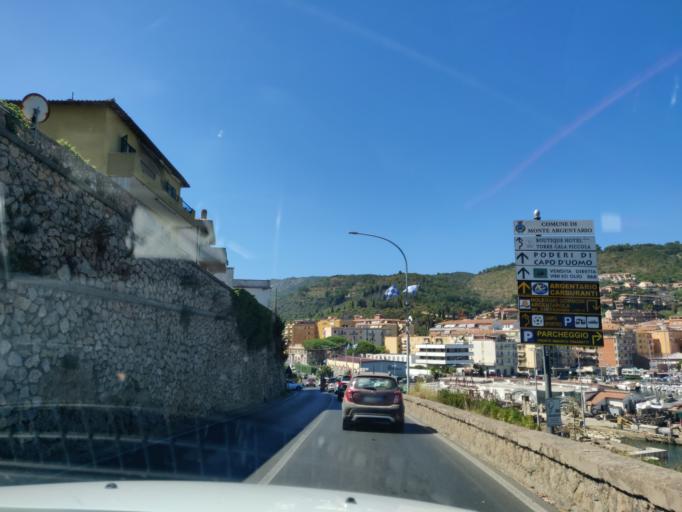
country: IT
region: Tuscany
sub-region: Provincia di Grosseto
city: Monte Argentario
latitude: 42.4353
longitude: 11.1253
